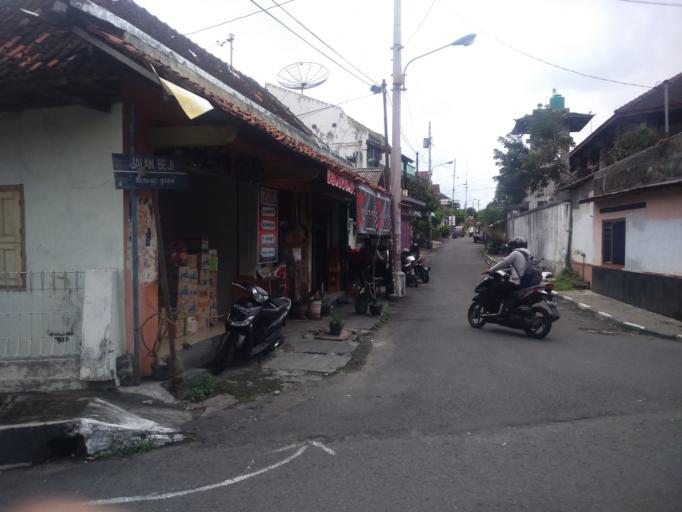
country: ID
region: Daerah Istimewa Yogyakarta
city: Yogyakarta
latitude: -7.8009
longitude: 110.3713
